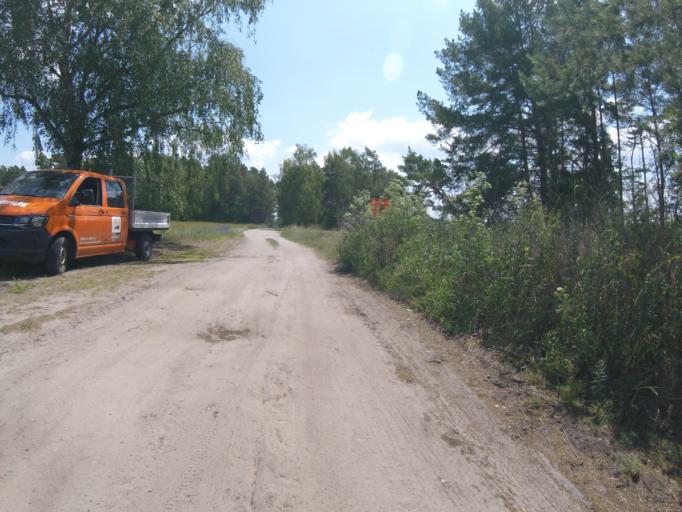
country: DE
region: Brandenburg
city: Bestensee
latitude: 52.2810
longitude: 13.6767
